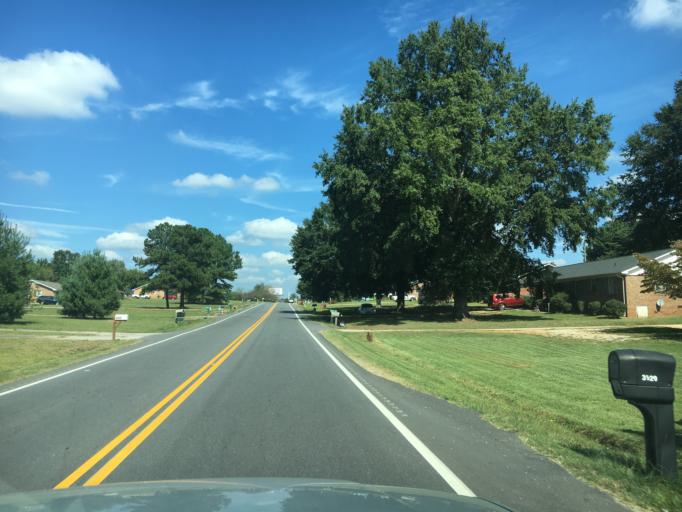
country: US
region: South Carolina
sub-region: Spartanburg County
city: Valley Falls
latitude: 35.0196
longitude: -81.9495
